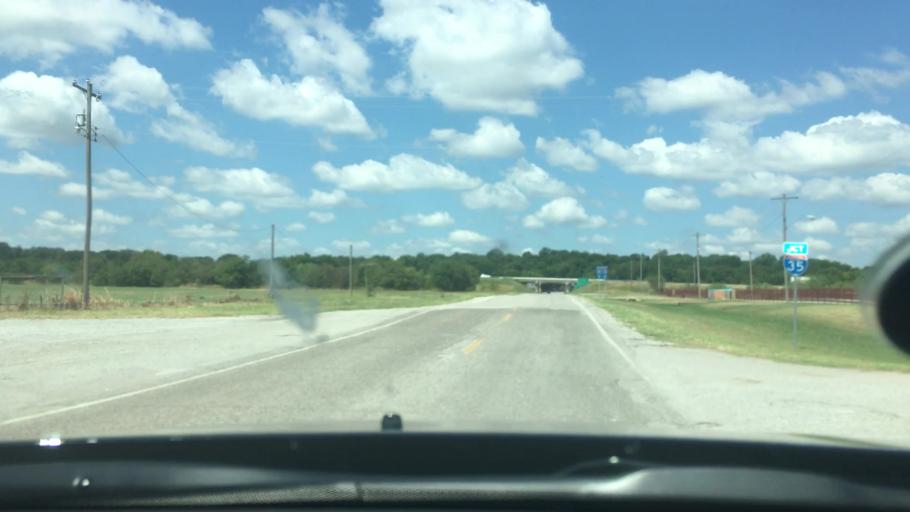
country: US
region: Oklahoma
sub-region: Carter County
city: Ardmore
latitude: 34.0710
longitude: -97.1451
